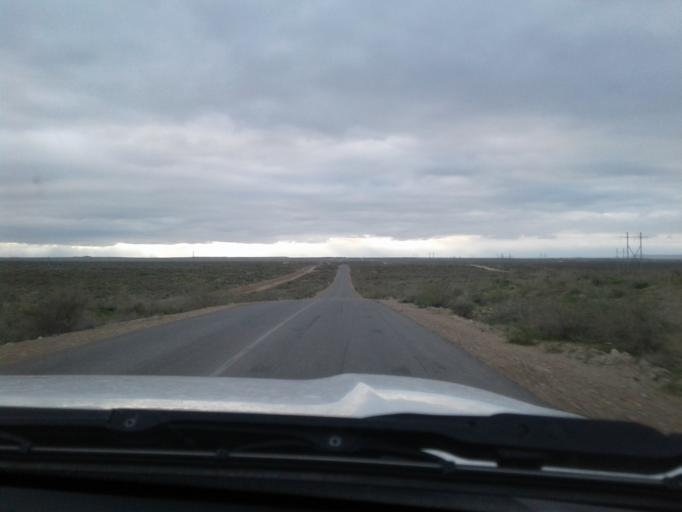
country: TM
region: Lebap
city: Sayat
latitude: 38.9105
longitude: 64.3330
